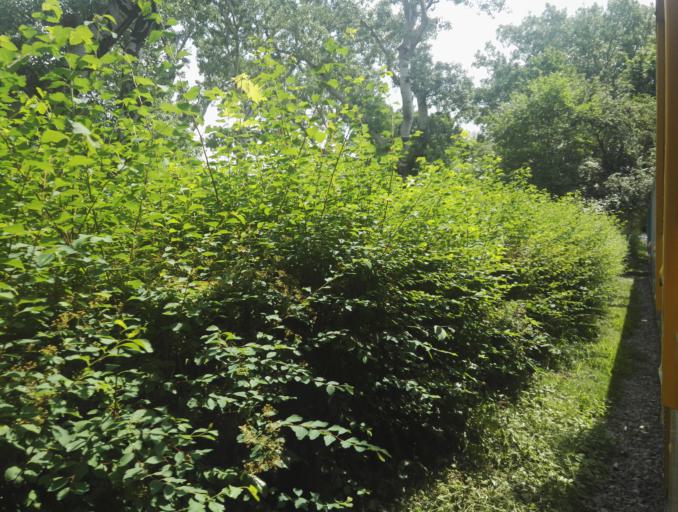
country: AT
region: Vienna
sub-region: Wien Stadt
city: Vienna
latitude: 48.2380
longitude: 16.4151
